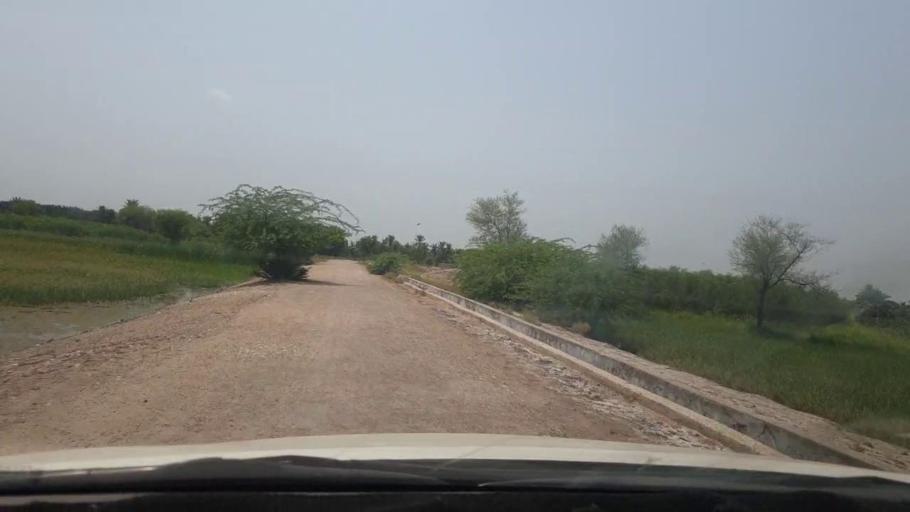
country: PK
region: Sindh
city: Khairpur
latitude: 27.5111
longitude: 68.8145
